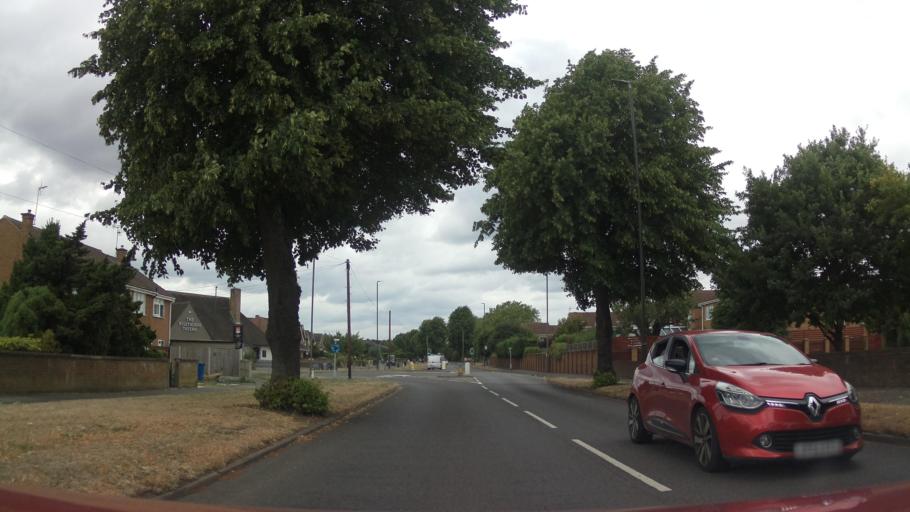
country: GB
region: England
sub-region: Derbyshire
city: Long Eaton
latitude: 52.8895
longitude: -1.2891
